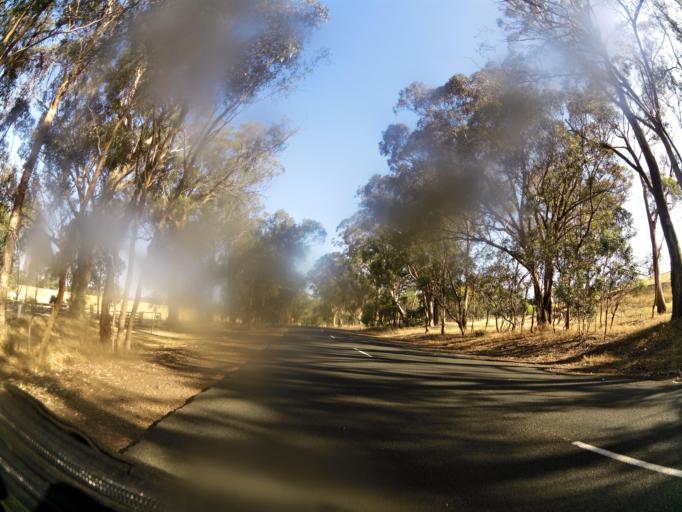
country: AU
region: Victoria
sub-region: Murrindindi
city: Kinglake West
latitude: -37.0057
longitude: 145.1226
